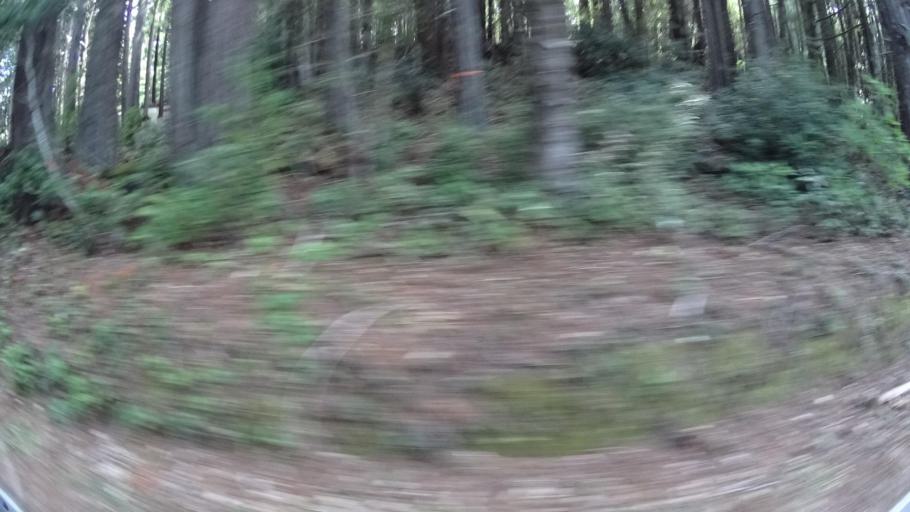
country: US
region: California
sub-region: Humboldt County
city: Bayside
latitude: 40.7591
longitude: -123.9929
